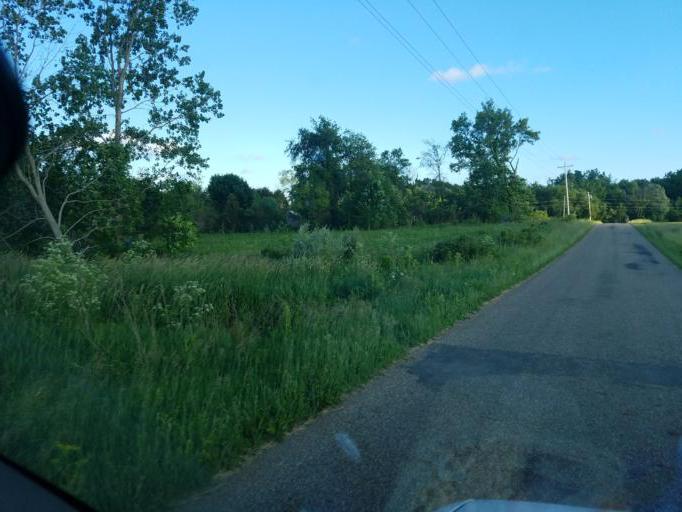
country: US
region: Ohio
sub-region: Knox County
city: Fredericktown
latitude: 40.4398
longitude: -82.6290
